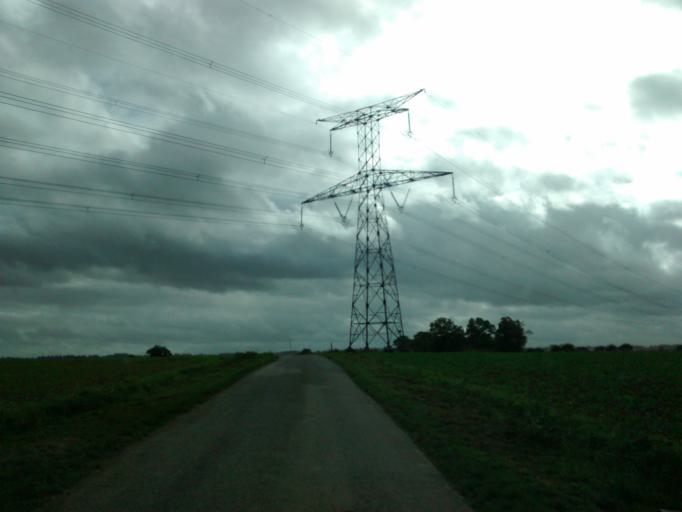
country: FR
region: Brittany
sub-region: Departement d'Ille-et-Vilaine
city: Chateaubourg
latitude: 48.1206
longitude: -1.4170
